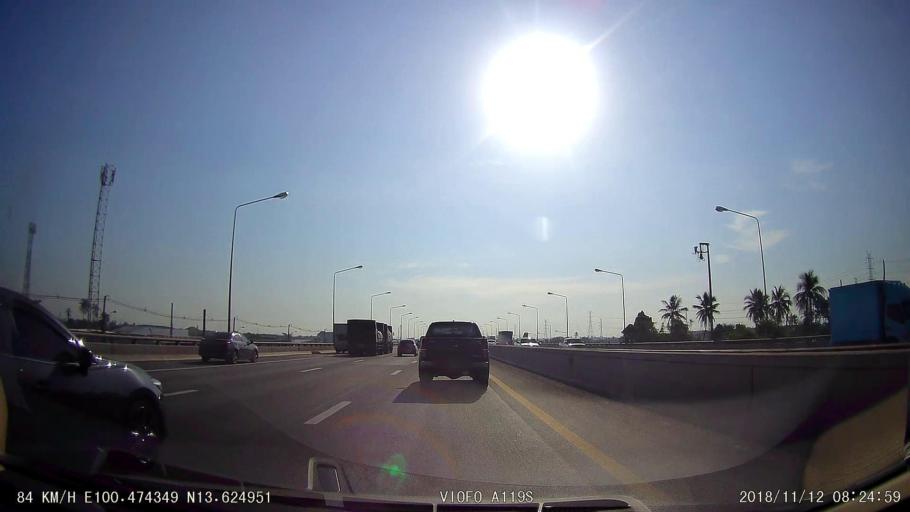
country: TH
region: Bangkok
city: Thung Khru
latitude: 13.6248
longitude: 100.4747
